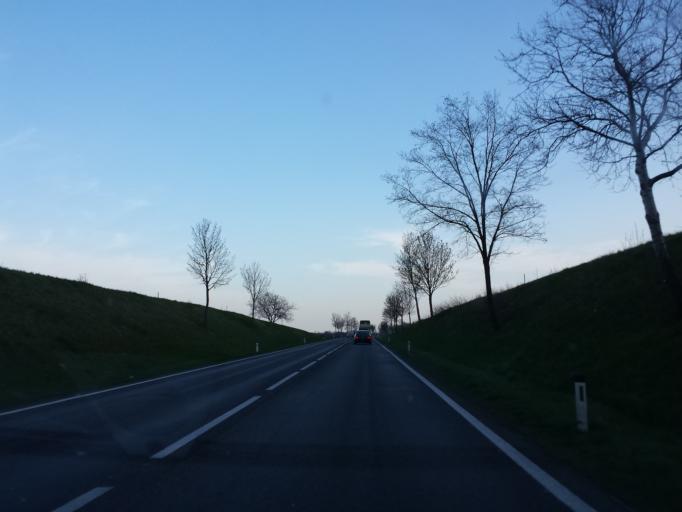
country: AT
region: Lower Austria
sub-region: Politischer Bezirk Mistelbach
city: Poysdorf
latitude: 48.6464
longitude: 16.6351
